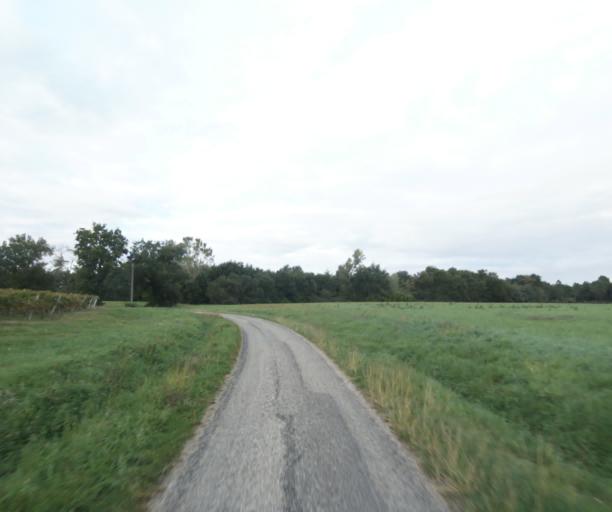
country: FR
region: Aquitaine
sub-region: Departement des Landes
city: Gabarret
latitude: 43.9762
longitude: 0.1038
